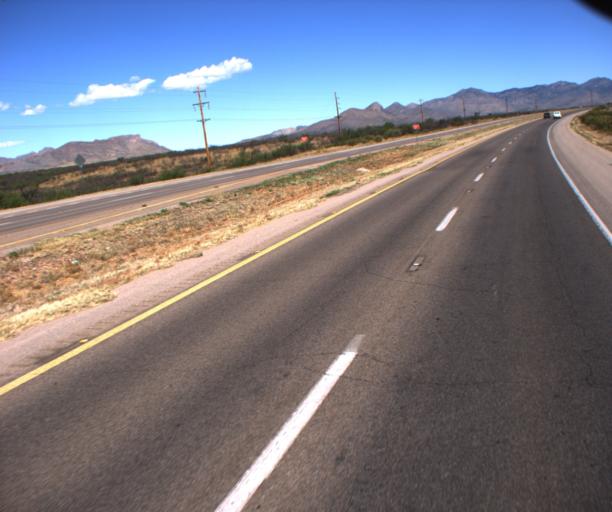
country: US
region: Arizona
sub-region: Cochise County
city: Huachuca City
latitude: 31.6574
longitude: -110.3478
